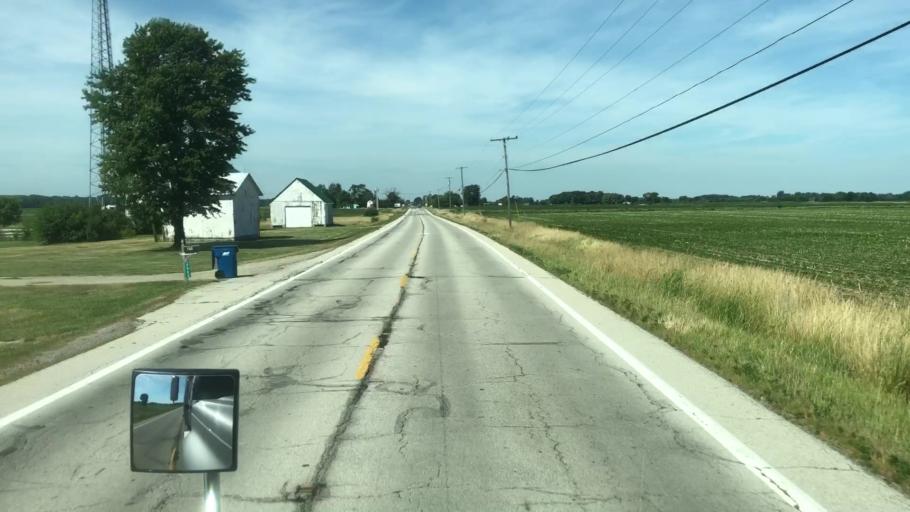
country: US
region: Ohio
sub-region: Ottawa County
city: Port Clinton
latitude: 41.4287
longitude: -82.8548
